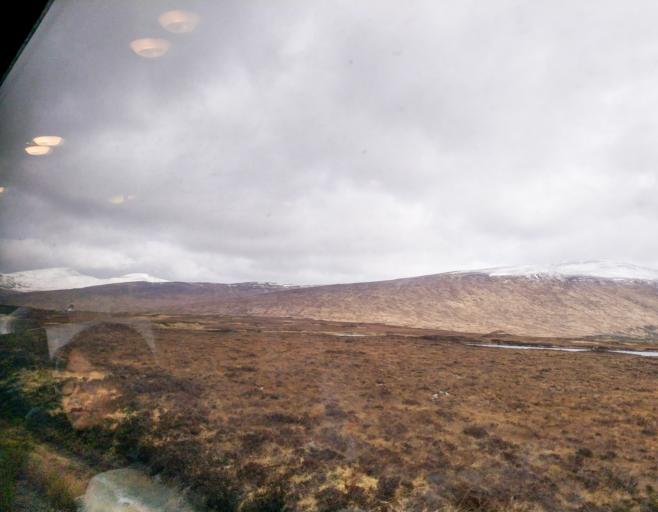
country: GB
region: Scotland
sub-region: Highland
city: Spean Bridge
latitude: 56.7521
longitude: -4.6787
